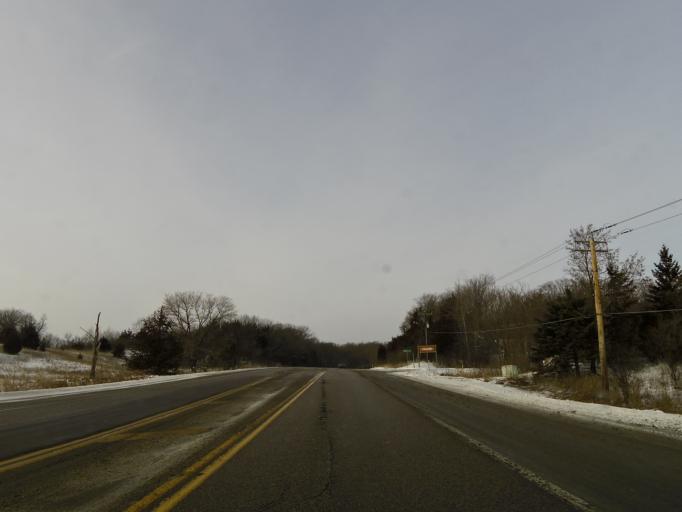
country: US
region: Minnesota
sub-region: Carver County
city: Victoria
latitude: 44.8866
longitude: -93.6527
